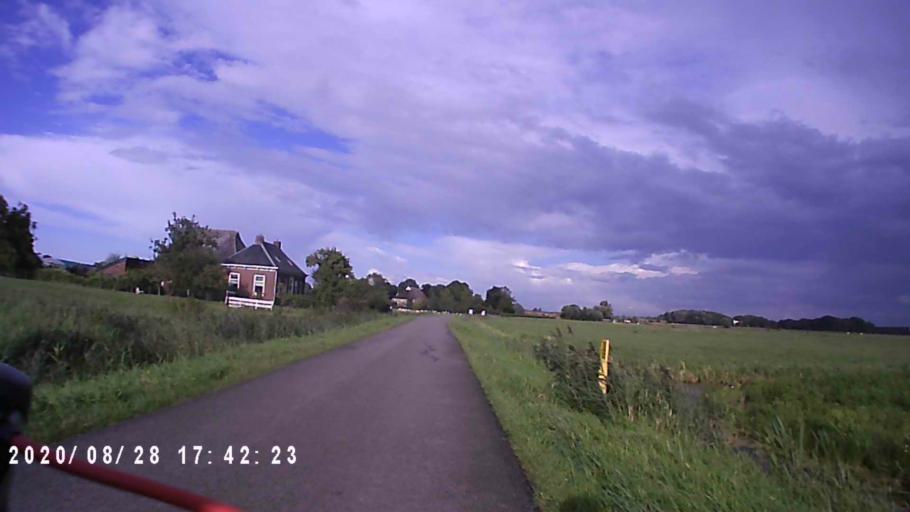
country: NL
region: Groningen
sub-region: Gemeente Zuidhorn
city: Aduard
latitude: 53.2480
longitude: 6.5076
